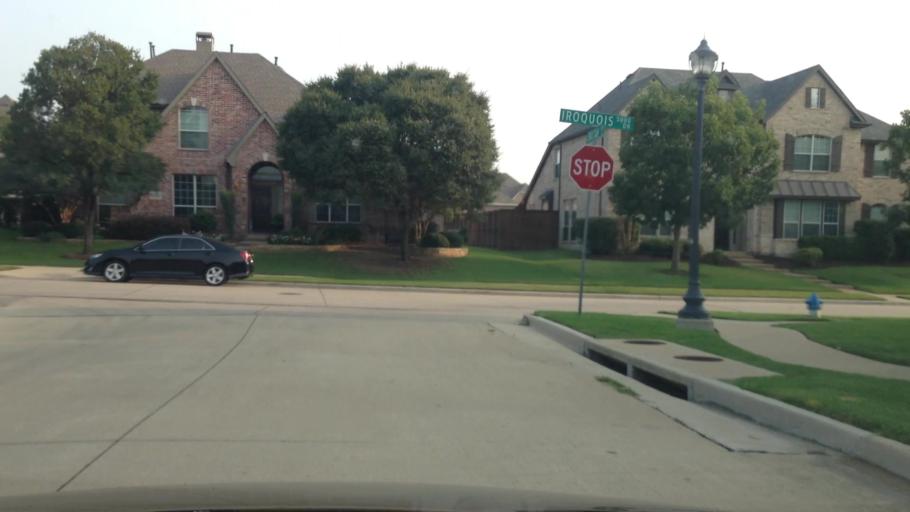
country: US
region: Texas
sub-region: Collin County
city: Frisco
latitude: 33.1277
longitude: -96.8448
